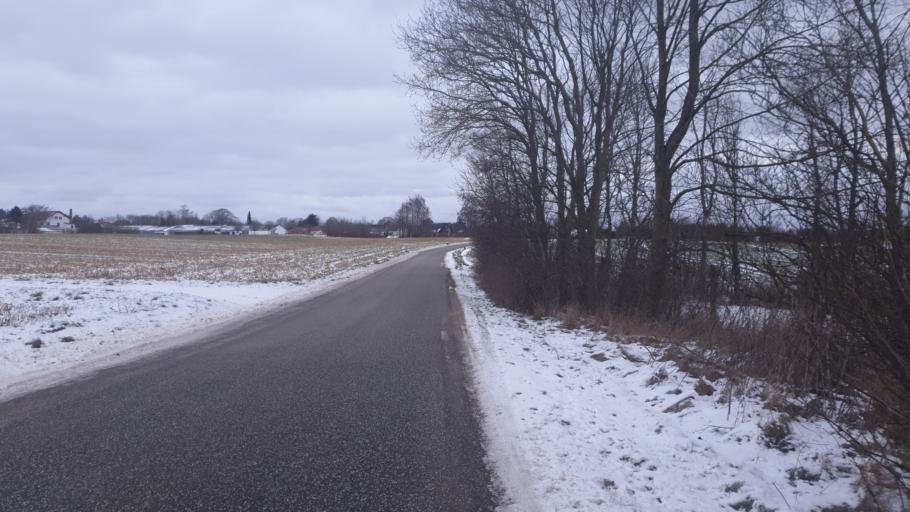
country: DK
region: Central Jutland
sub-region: Hedensted Kommune
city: Hedensted
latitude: 55.7991
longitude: 9.7060
